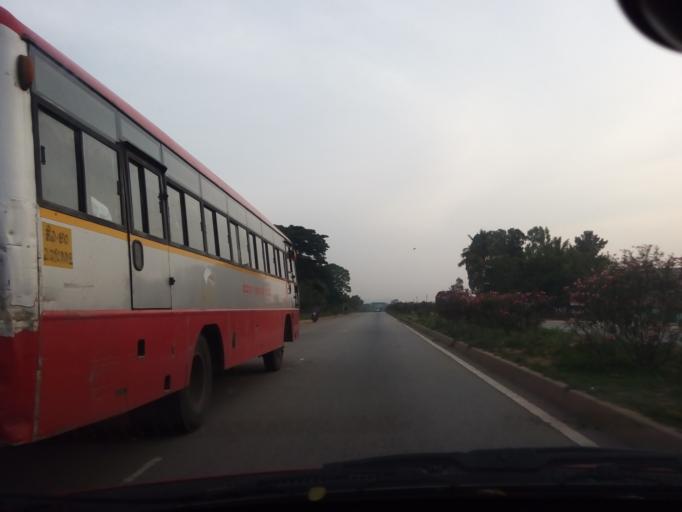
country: IN
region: Karnataka
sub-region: Chikkaballapur
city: Chik Ballapur
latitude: 13.3749
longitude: 77.7260
